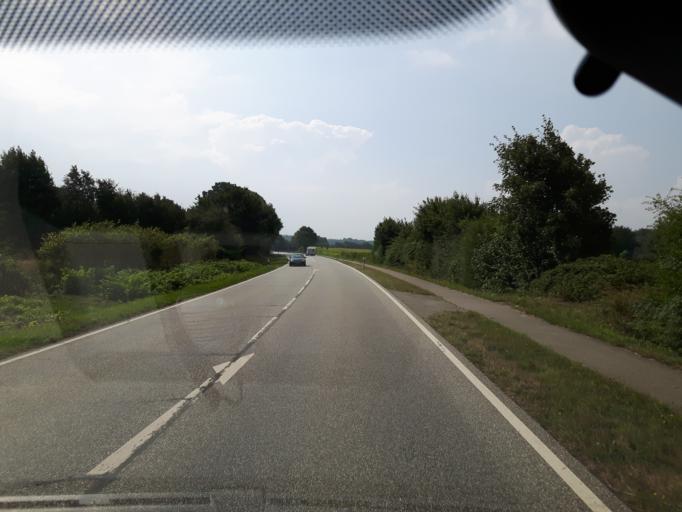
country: DE
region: Schleswig-Holstein
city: Goosefeld
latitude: 54.4197
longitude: 9.8016
